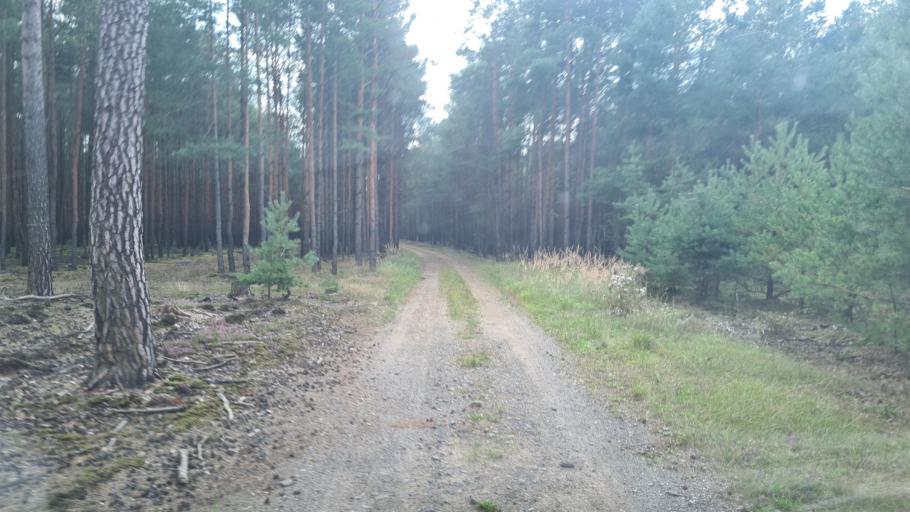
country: DE
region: Brandenburg
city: Schonewalde
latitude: 51.7523
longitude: 13.6006
